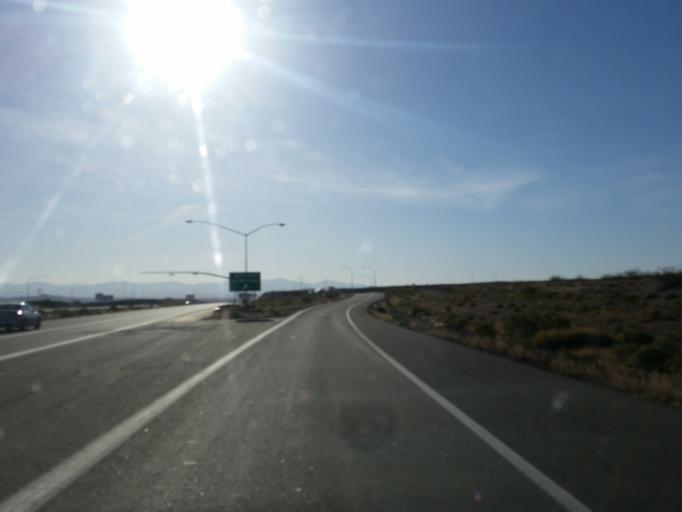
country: US
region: Arizona
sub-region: Mohave County
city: Desert Hills
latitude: 34.7230
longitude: -114.4255
